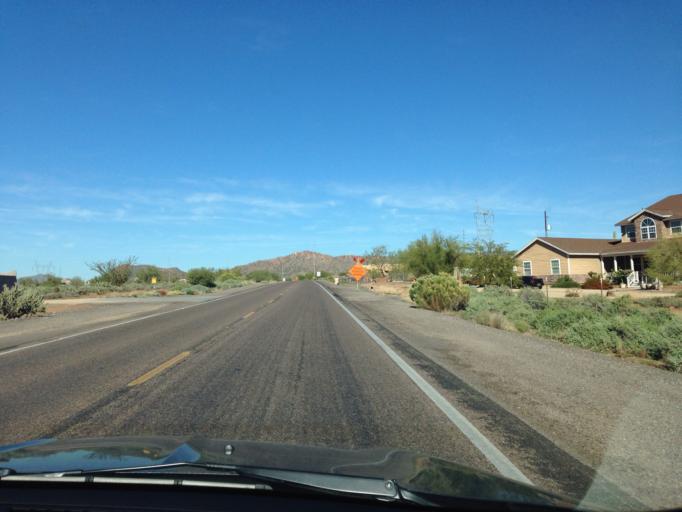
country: US
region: Arizona
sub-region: Maricopa County
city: Anthem
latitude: 33.8453
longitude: -112.0633
